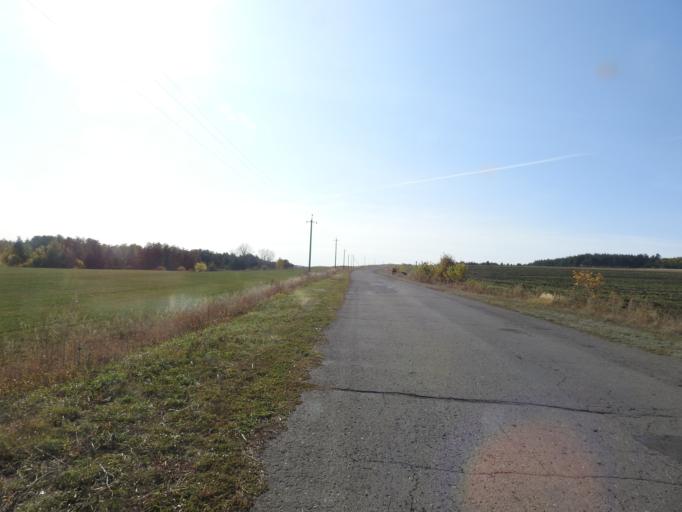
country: RU
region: Saratov
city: Baltay
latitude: 52.4694
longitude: 46.6671
